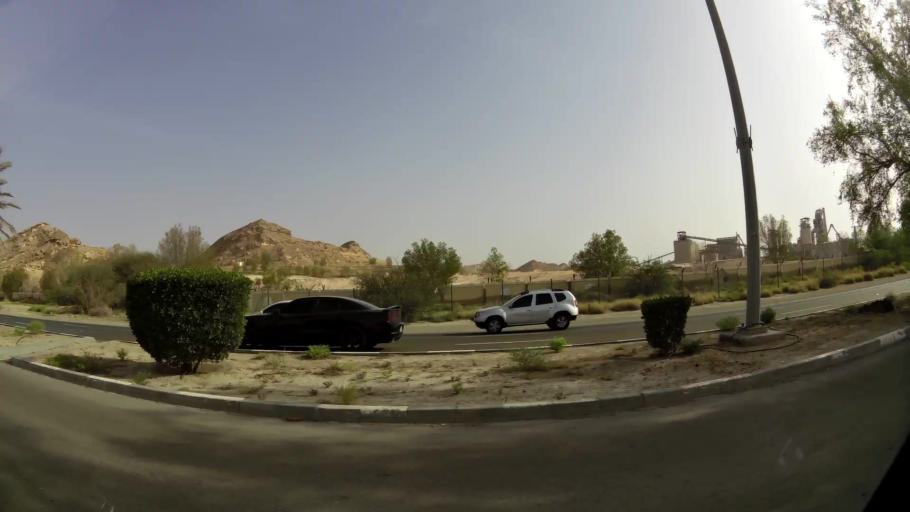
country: AE
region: Abu Dhabi
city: Al Ain
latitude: 24.1325
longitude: 55.7310
